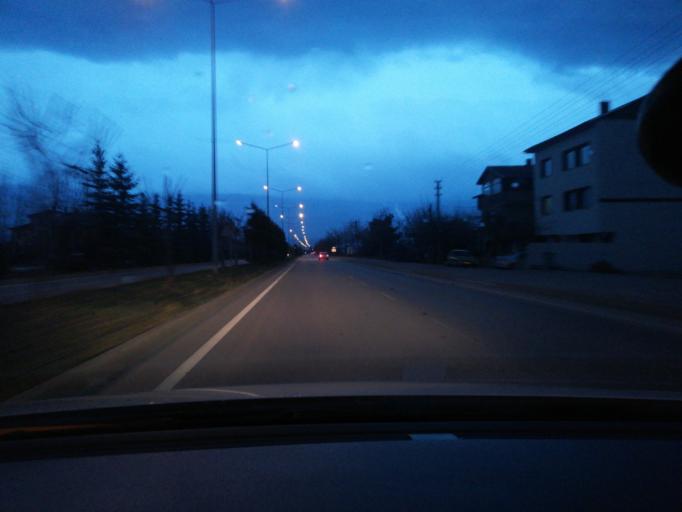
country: TR
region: Bolu
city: Bolu
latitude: 40.7219
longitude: 31.6130
